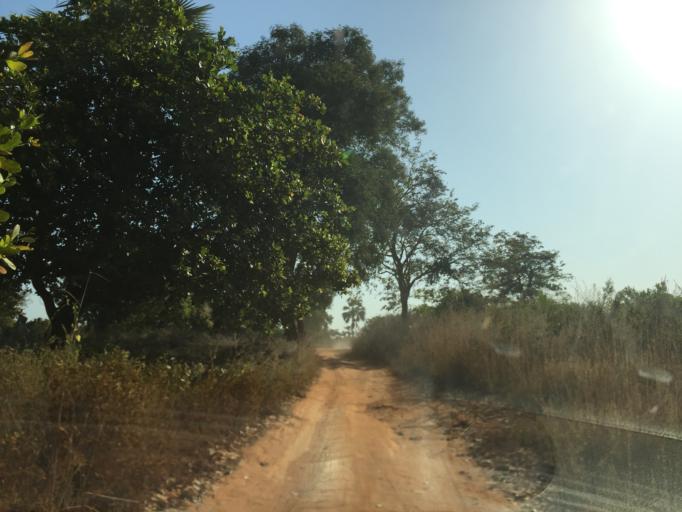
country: GW
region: Oio
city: Farim
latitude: 12.4560
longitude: -15.3069
